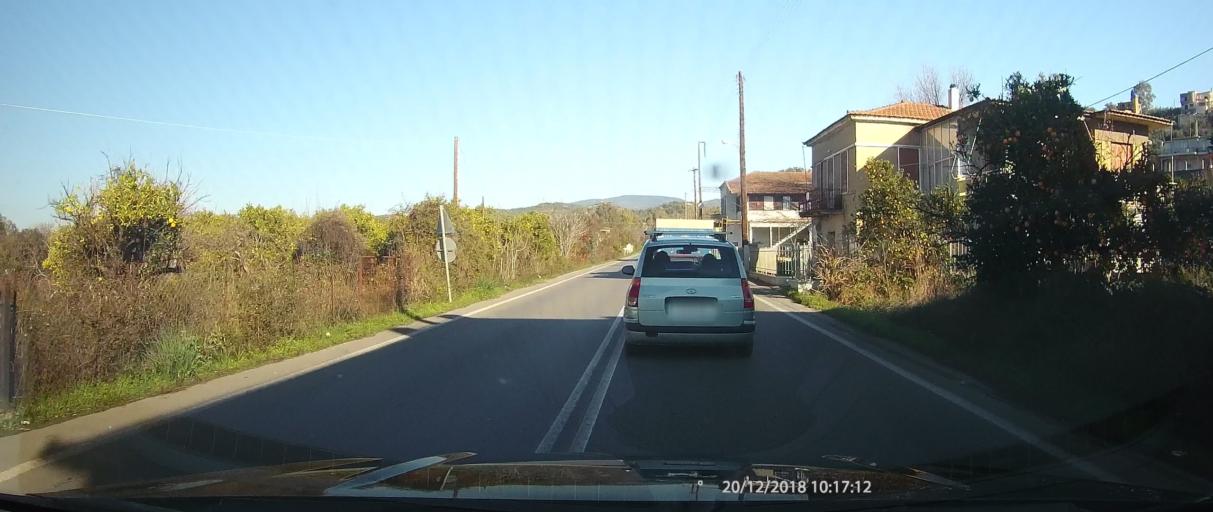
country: GR
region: Peloponnese
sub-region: Nomos Lakonias
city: Sparti
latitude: 37.1038
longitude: 22.4340
